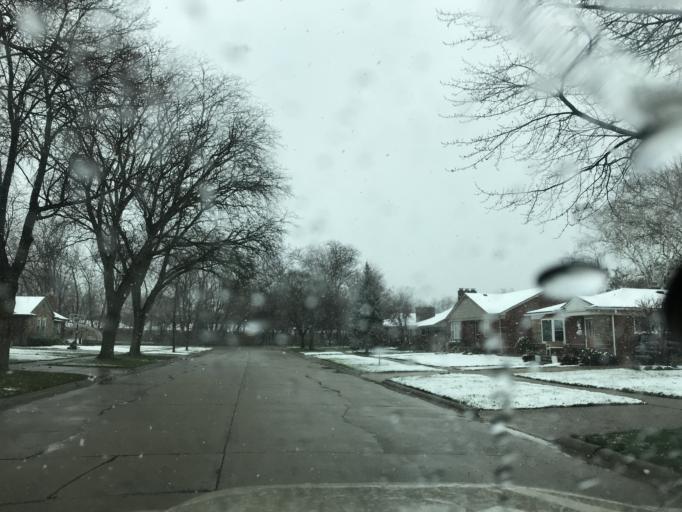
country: US
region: Michigan
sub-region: Wayne County
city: Allen Park
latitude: 42.2348
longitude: -83.2186
